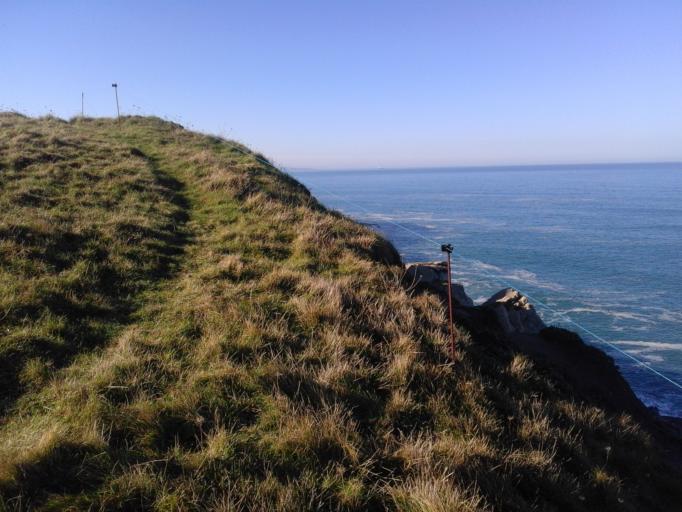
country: ES
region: Cantabria
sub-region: Provincia de Cantabria
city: Arnuero
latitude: 43.5129
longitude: -3.5898
